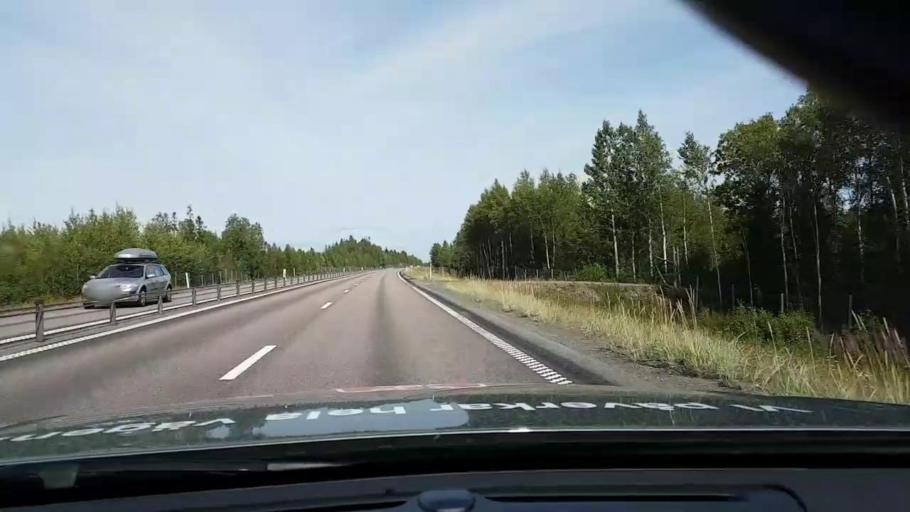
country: SE
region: Vaesternorrland
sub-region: OErnskoeldsviks Kommun
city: Husum
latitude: 63.4443
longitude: 19.2174
